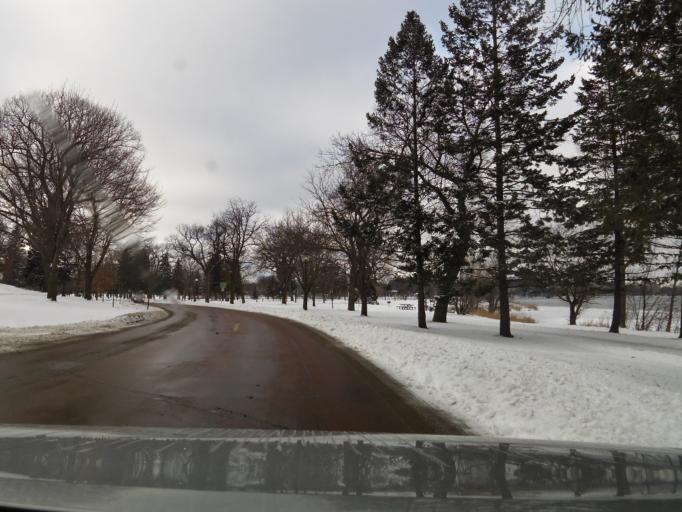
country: US
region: Minnesota
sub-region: Hennepin County
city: Saint Louis Park
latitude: 44.9351
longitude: -93.3140
